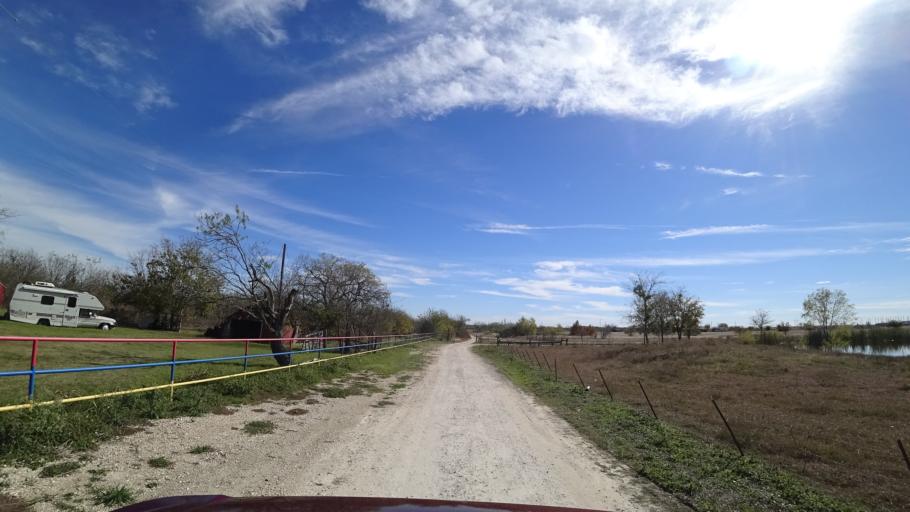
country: US
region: Texas
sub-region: Travis County
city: Onion Creek
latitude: 30.1159
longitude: -97.6827
